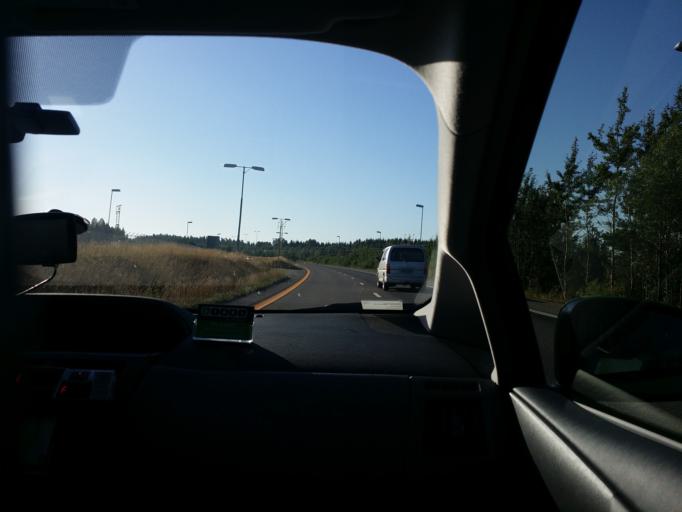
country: NO
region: Akershus
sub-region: Ullensaker
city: Jessheim
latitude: 60.1708
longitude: 11.1027
